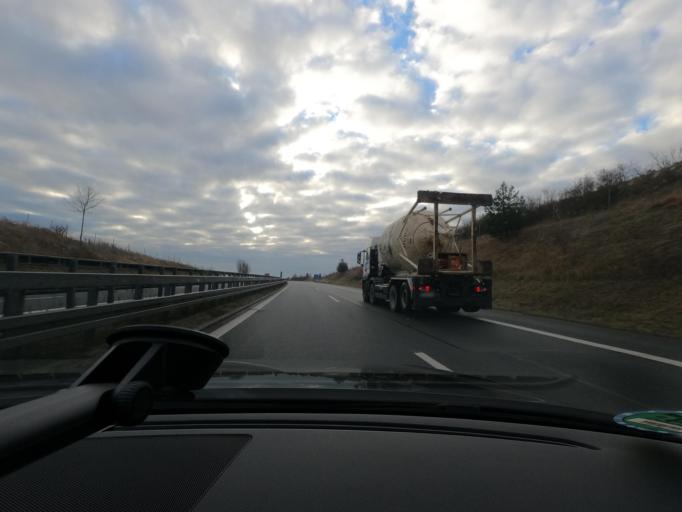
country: DE
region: Bavaria
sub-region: Upper Franconia
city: Rodental
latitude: 50.2610
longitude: 11.0188
